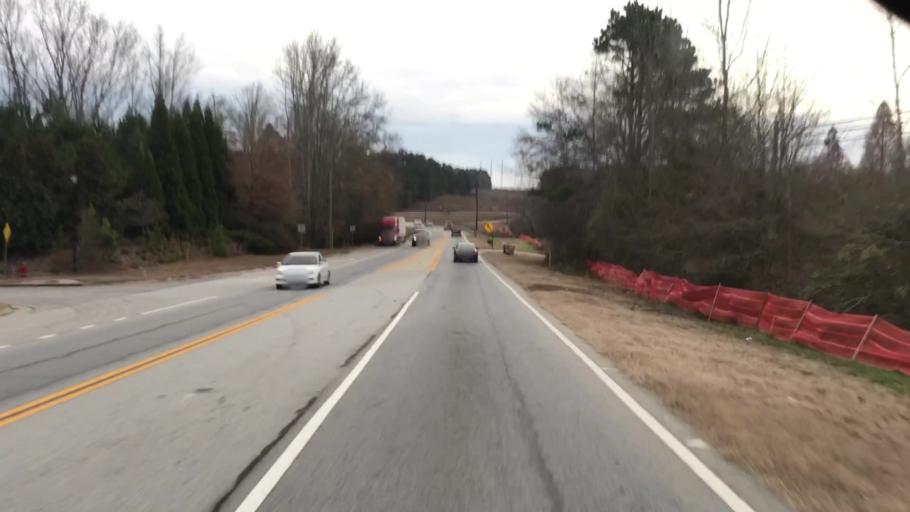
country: US
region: Georgia
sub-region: Barrow County
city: Winder
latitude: 34.0088
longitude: -83.7563
